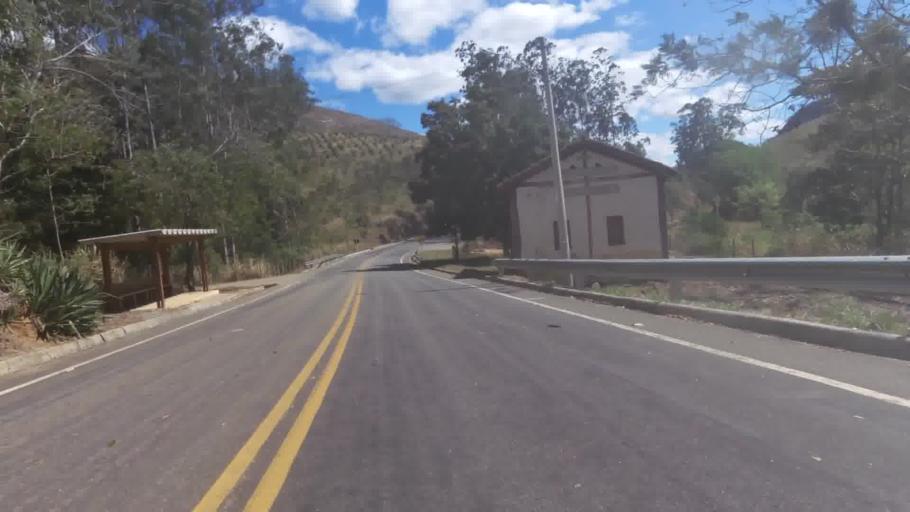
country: BR
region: Espirito Santo
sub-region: Cachoeiro De Itapemirim
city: Cachoeiro de Itapemirim
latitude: -20.9118
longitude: -41.2413
